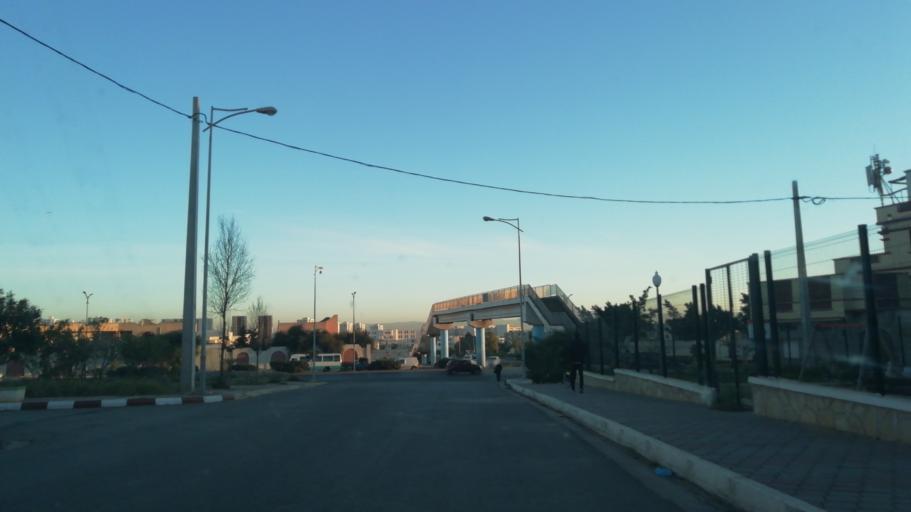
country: DZ
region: Oran
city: Bir el Djir
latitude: 35.7107
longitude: -0.5867
